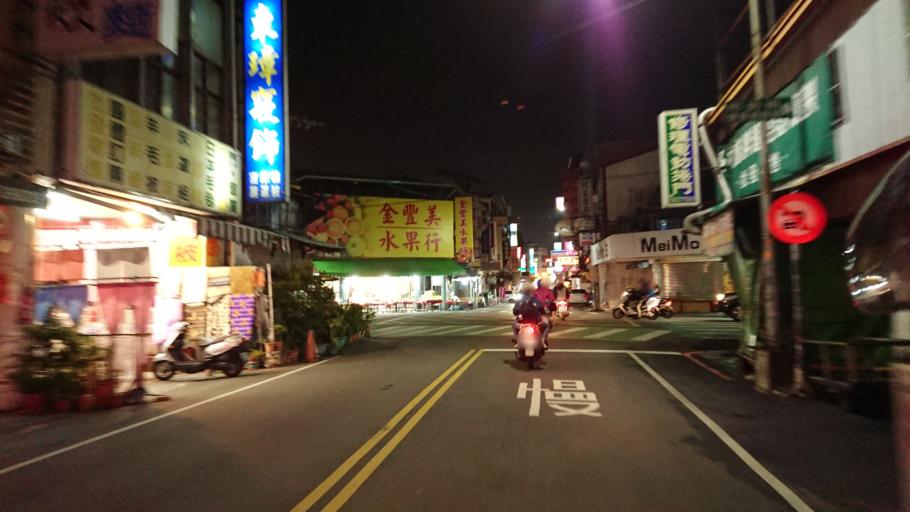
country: TW
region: Taiwan
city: Fengyuan
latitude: 24.2492
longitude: 120.7154
